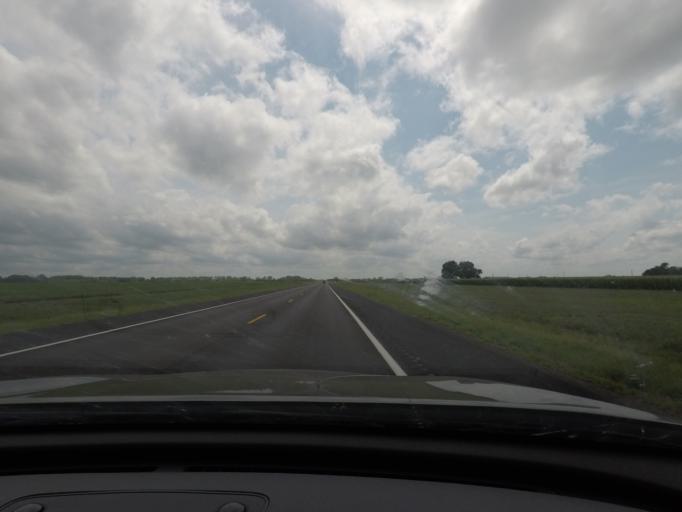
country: US
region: Missouri
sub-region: Carroll County
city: Carrollton
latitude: 39.2922
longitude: -93.5069
